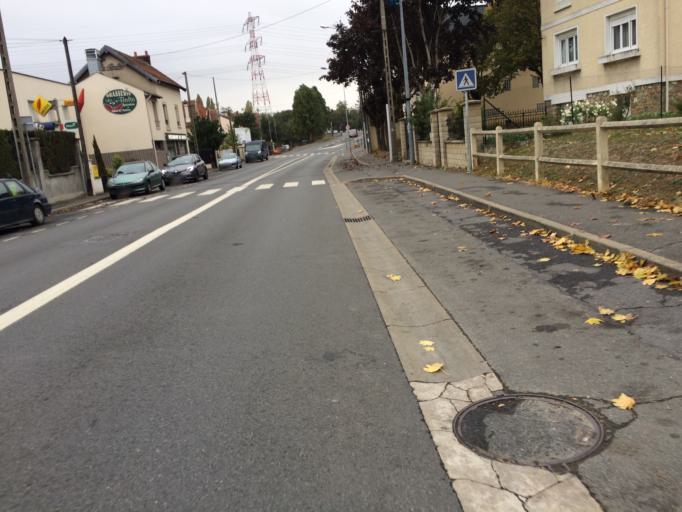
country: FR
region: Ile-de-France
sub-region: Departement de l'Essonne
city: Palaiseau
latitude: 48.7149
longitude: 2.2569
